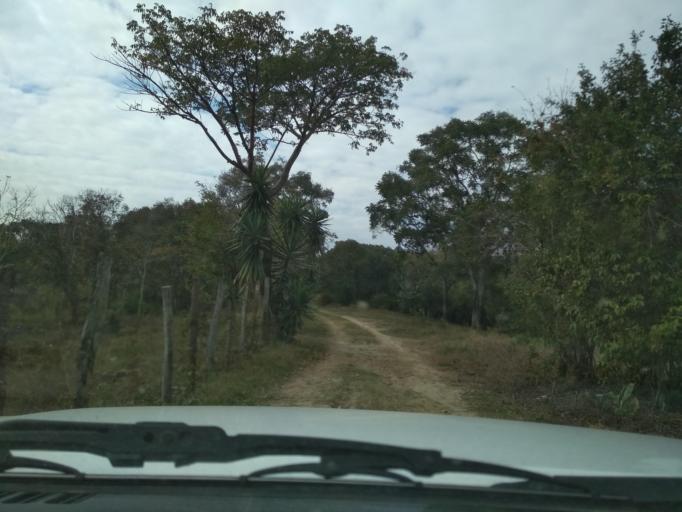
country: MX
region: Veracruz
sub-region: Coatepec
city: Tuzamapan
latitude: 19.3692
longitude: -96.8774
